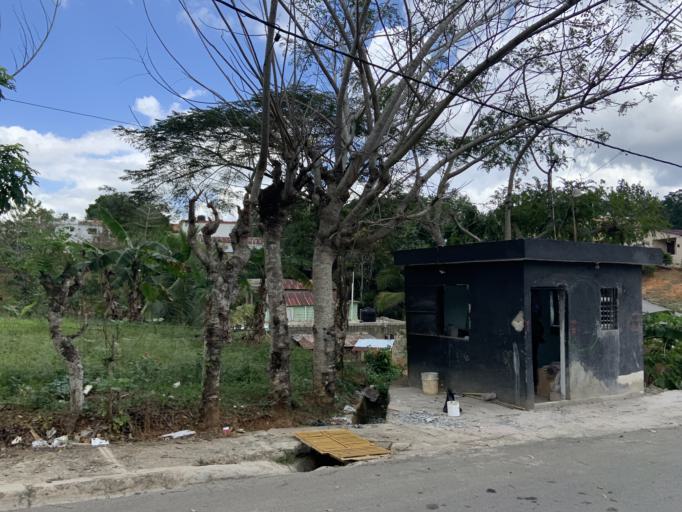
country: DO
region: Monte Plata
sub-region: Yamasa
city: Yamasa
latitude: 18.7705
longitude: -70.0227
